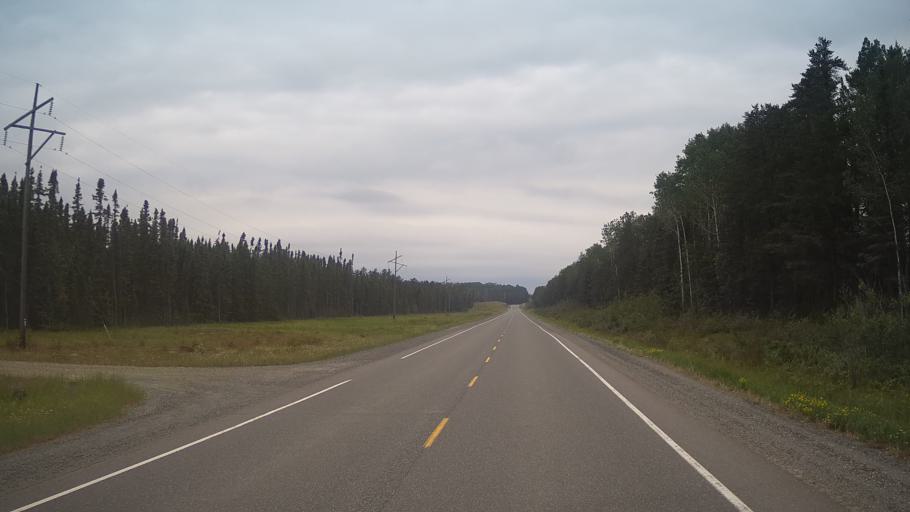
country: CA
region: Ontario
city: Greenstone
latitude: 49.6692
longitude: -87.7026
